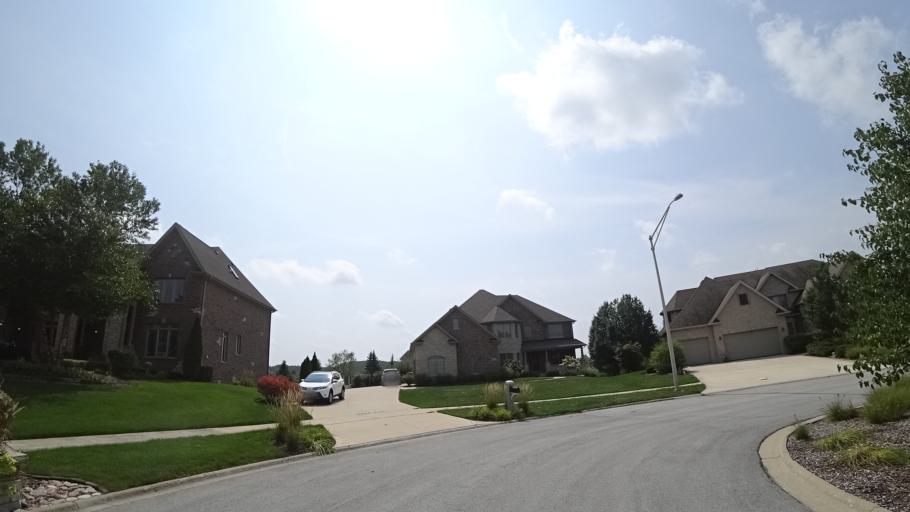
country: US
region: Illinois
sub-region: Cook County
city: Orland Park
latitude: 41.6328
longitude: -87.8844
